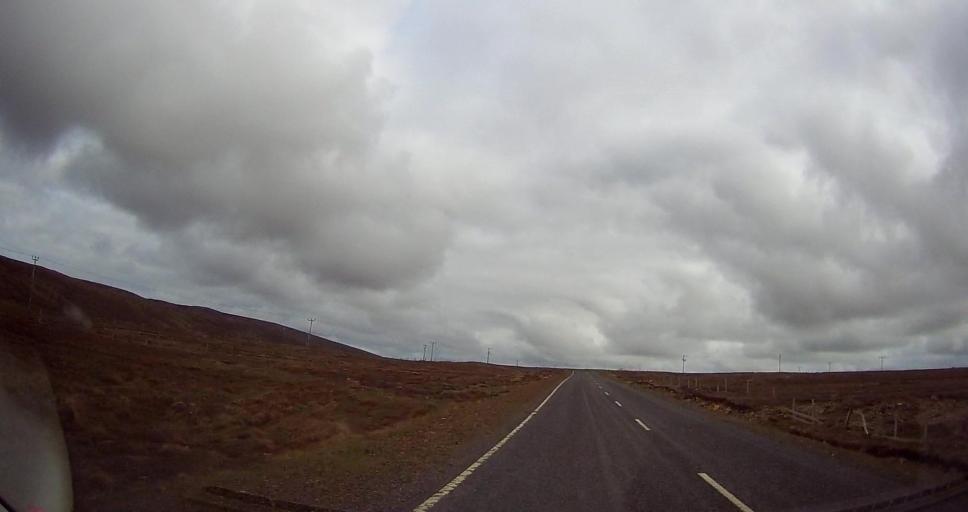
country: GB
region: Scotland
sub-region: Shetland Islands
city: Shetland
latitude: 60.7173
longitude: -0.9130
